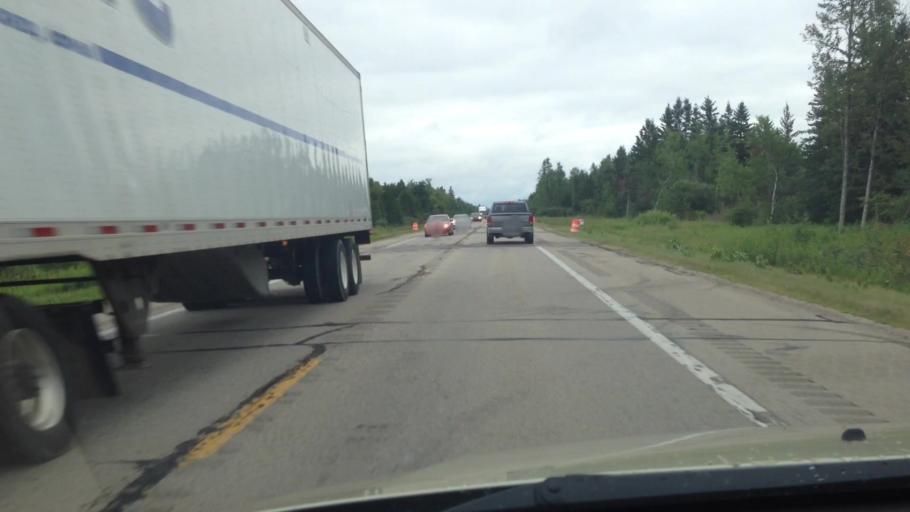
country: US
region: Michigan
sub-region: Delta County
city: Escanaba
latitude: 45.6094
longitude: -87.2191
